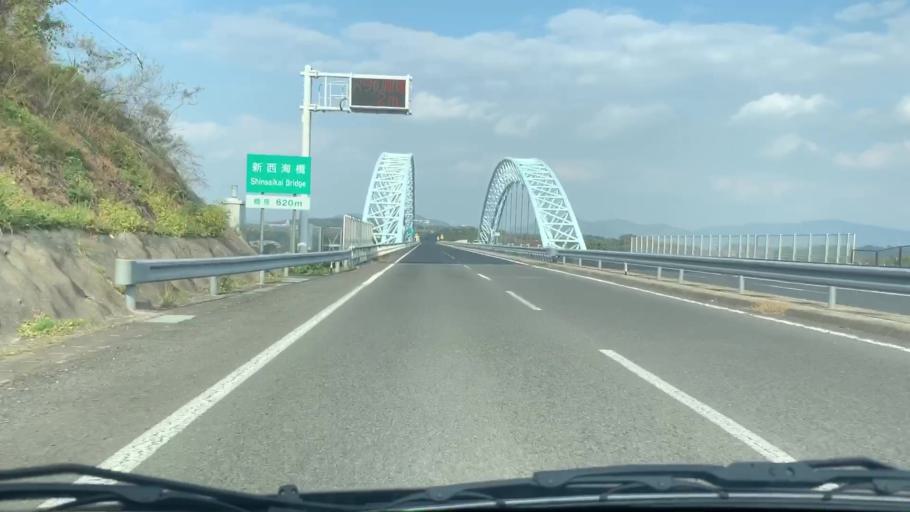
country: JP
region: Nagasaki
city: Sasebo
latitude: 33.0527
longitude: 129.7540
